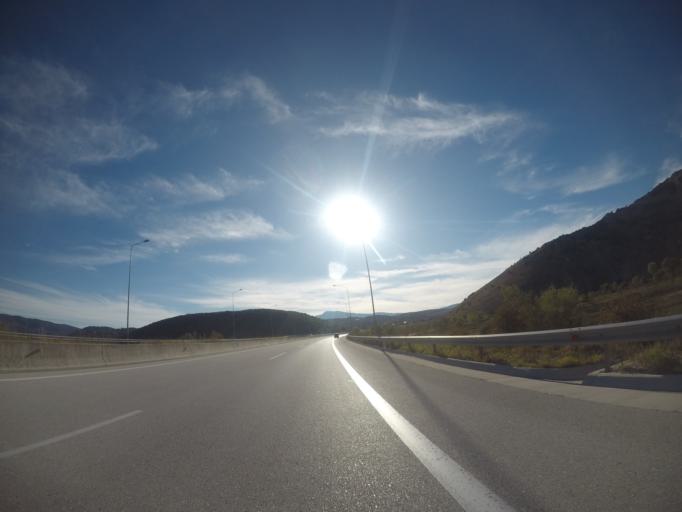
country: GR
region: Epirus
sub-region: Nomos Ioanninon
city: Koutselio
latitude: 39.5995
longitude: 20.9252
